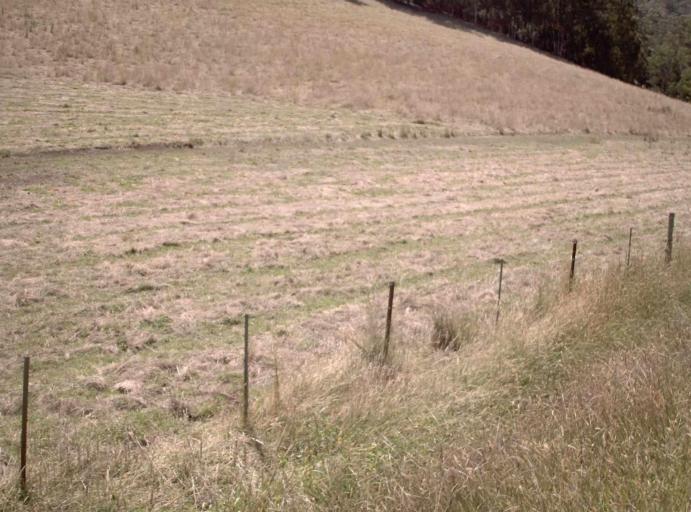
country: AU
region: Victoria
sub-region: Baw Baw
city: Warragul
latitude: -37.9044
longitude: 146.0225
